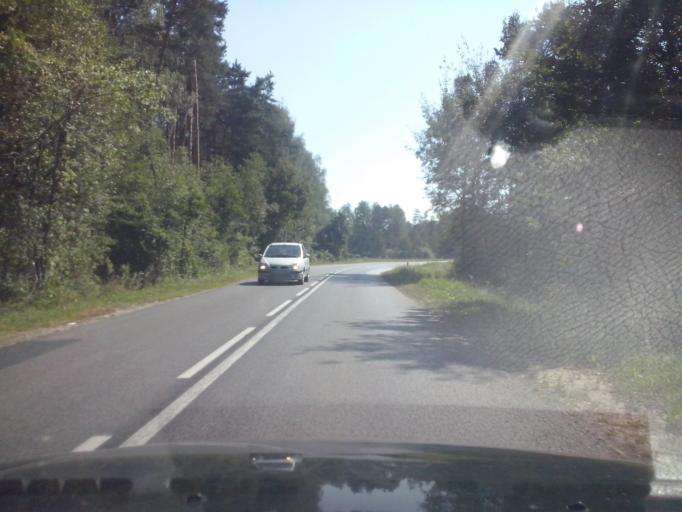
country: PL
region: Swietokrzyskie
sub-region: Powiat kielecki
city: Domaszowice
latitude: 50.8139
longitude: 20.7224
